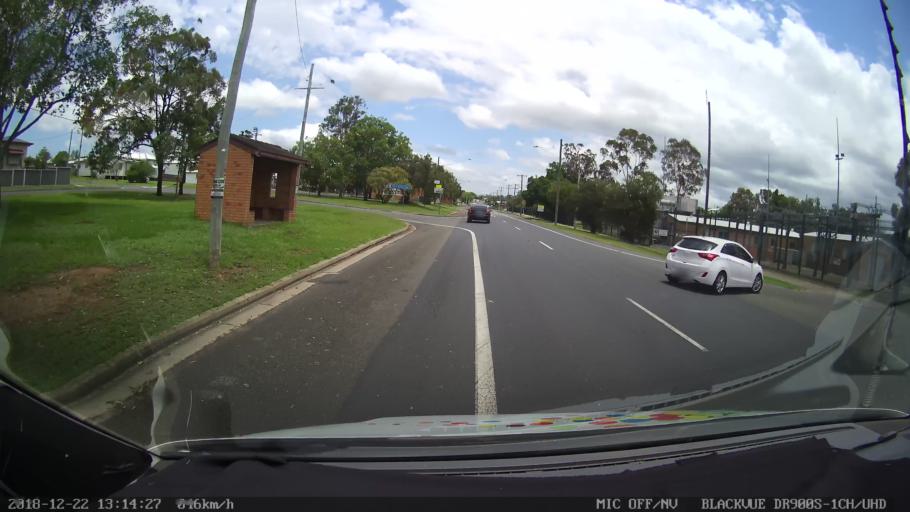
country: AU
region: New South Wales
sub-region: Clarence Valley
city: South Grafton
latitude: -29.7110
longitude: 152.9411
